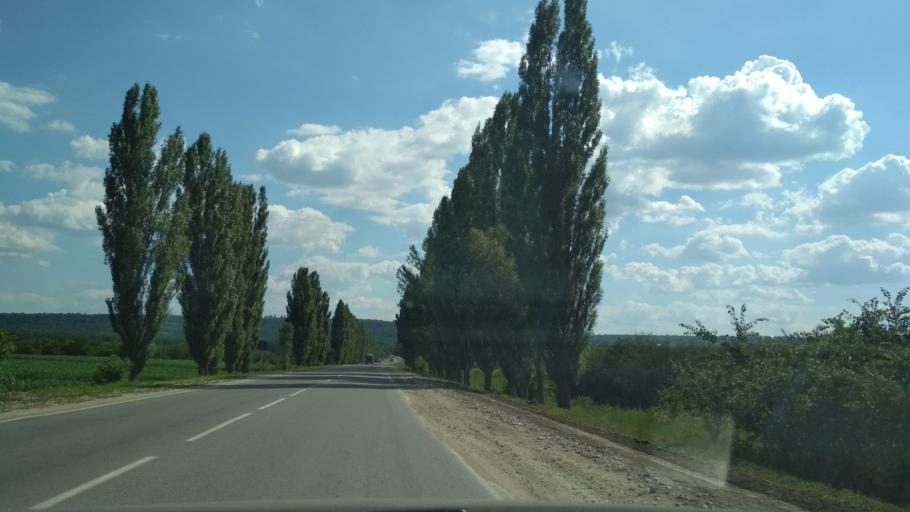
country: MD
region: Chisinau
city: Vadul lui Voda
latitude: 47.1006
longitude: 29.0981
